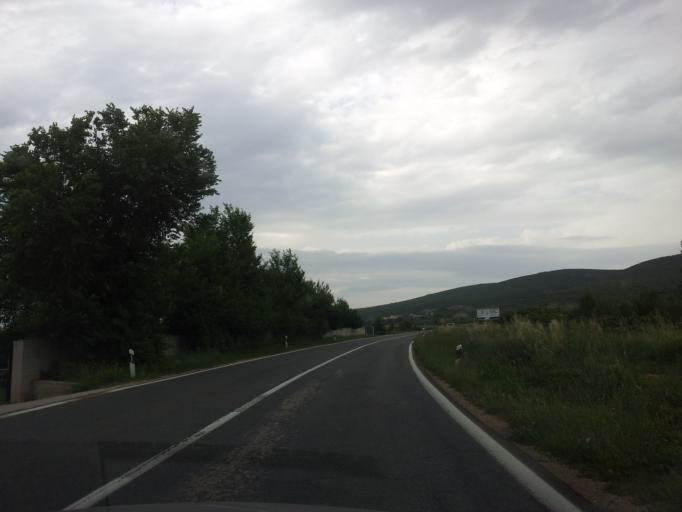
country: HR
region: Zadarska
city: Turanj
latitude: 43.9795
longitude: 15.3946
